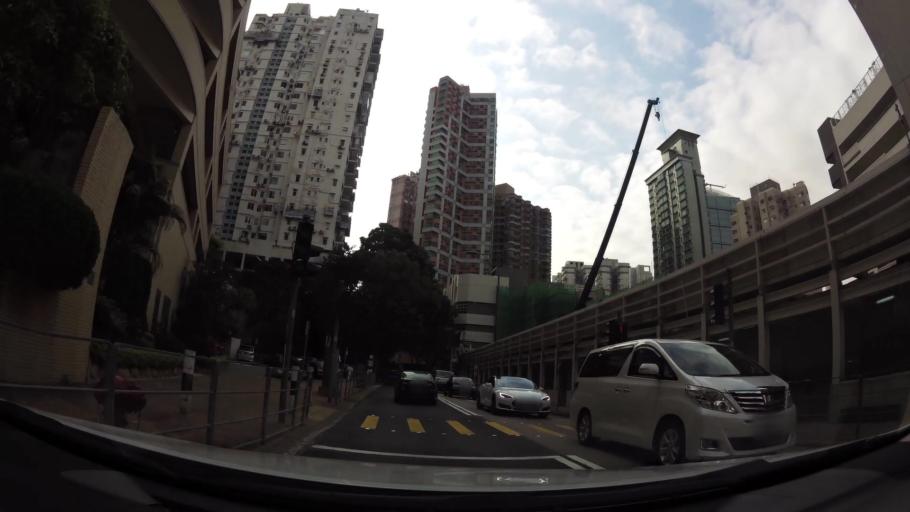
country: HK
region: Wanchai
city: Wan Chai
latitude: 22.2746
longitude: 114.1692
